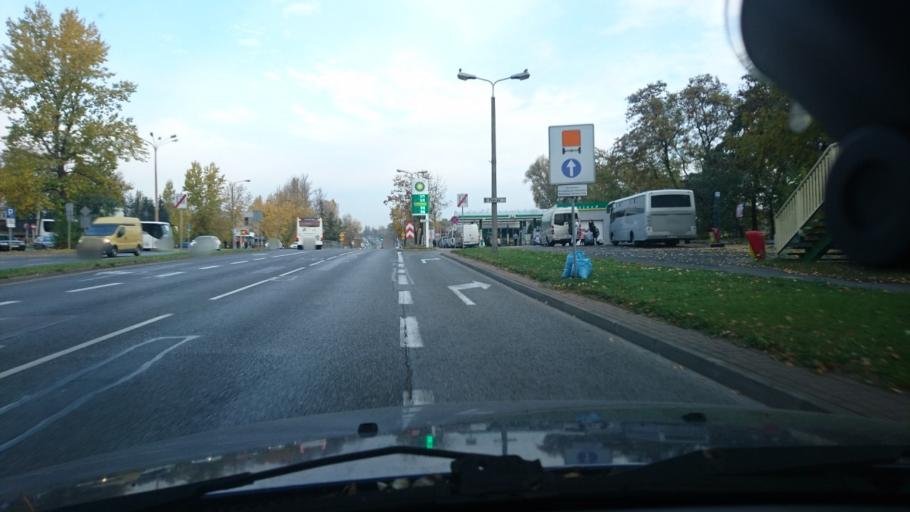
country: PL
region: Silesian Voivodeship
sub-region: Bielsko-Biala
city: Bielsko-Biala
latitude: 49.8305
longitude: 19.0441
